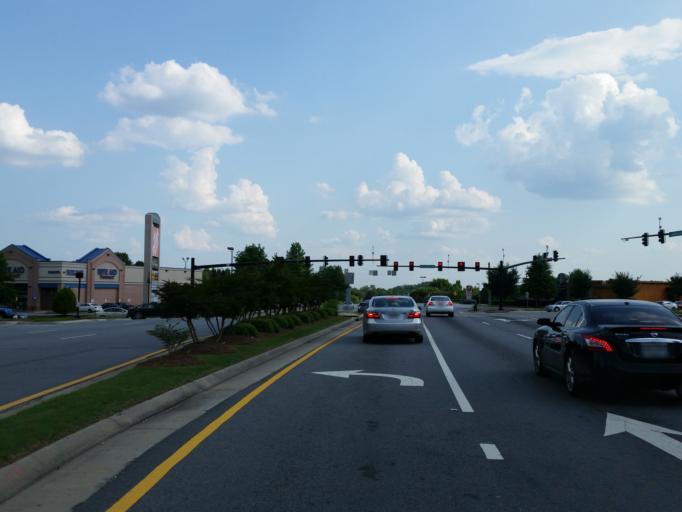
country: US
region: Georgia
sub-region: Cobb County
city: Vinings
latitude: 33.8662
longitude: -84.4766
